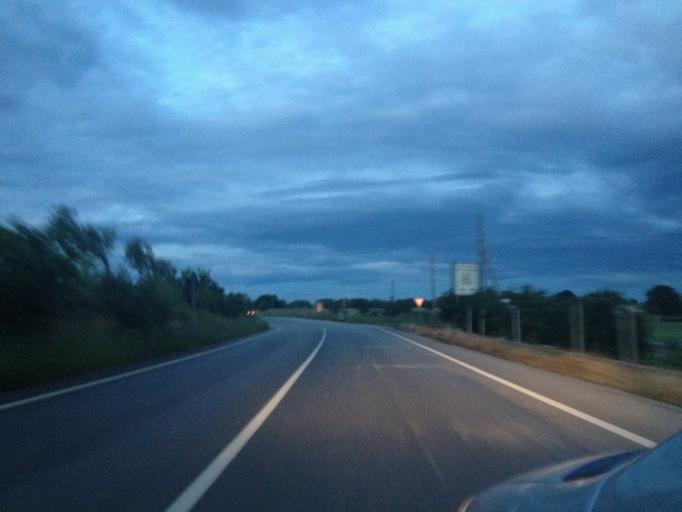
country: IT
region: Apulia
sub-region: Provincia di Bari
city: Alberobello
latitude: 40.8226
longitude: 17.2177
